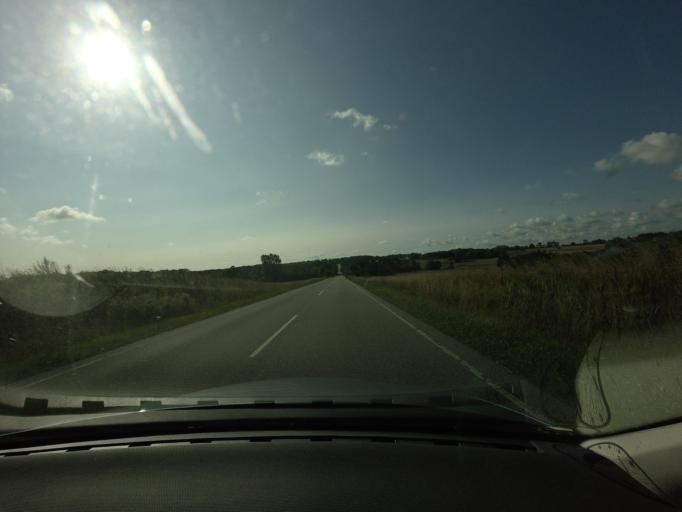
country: DK
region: Zealand
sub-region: Vordingborg Kommune
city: Praesto
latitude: 55.1039
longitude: 12.0710
